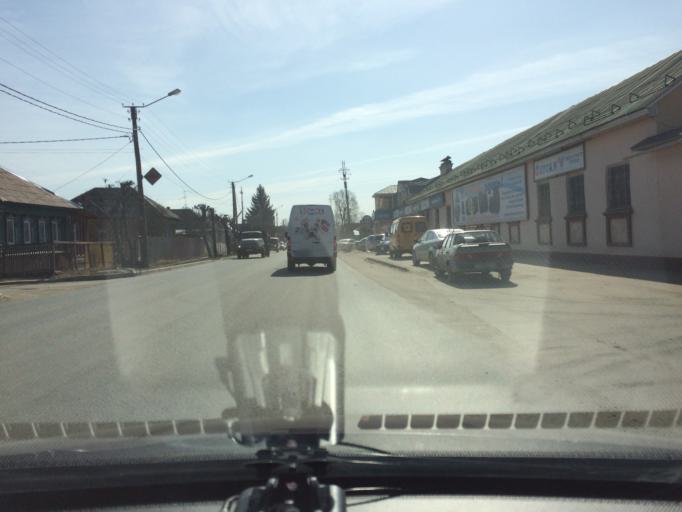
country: RU
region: Mariy-El
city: Yoshkar-Ola
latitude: 56.6481
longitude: 47.9036
